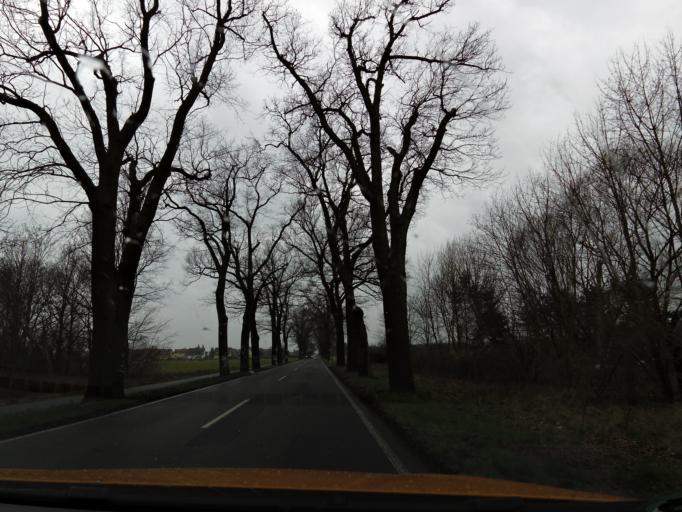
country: DE
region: Brandenburg
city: Brandenburg an der Havel
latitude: 52.4060
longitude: 12.5991
